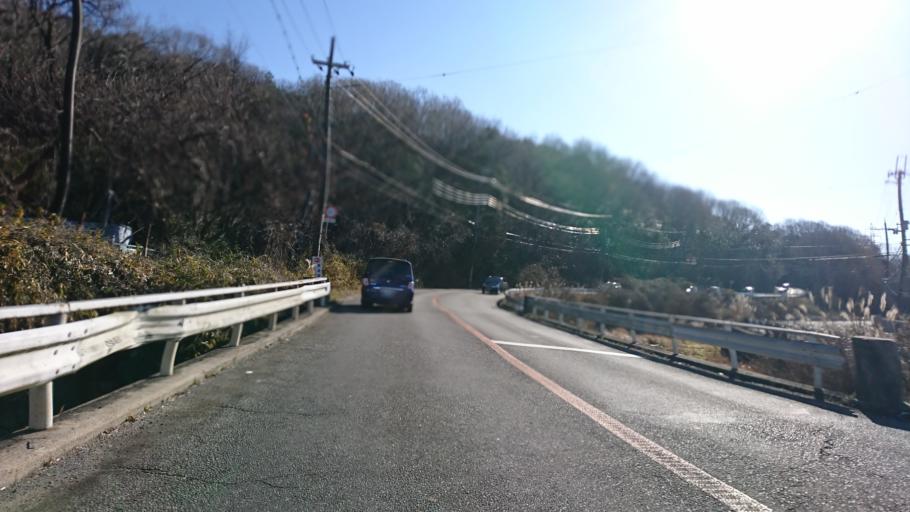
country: JP
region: Hyogo
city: Akashi
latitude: 34.7141
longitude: 134.9744
